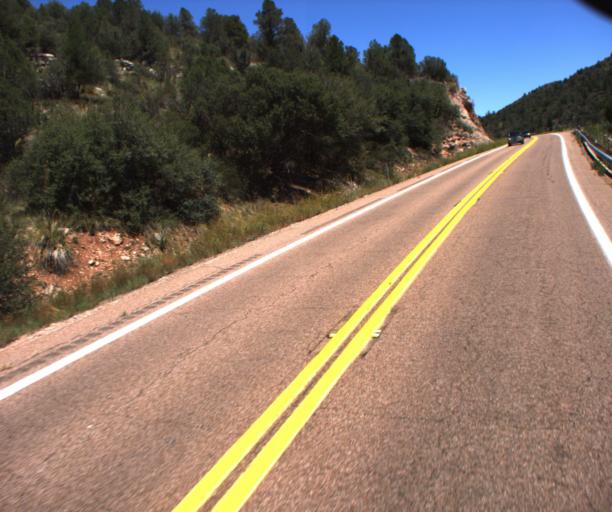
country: US
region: Arizona
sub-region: Navajo County
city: Cibecue
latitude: 33.8478
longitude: -110.4238
